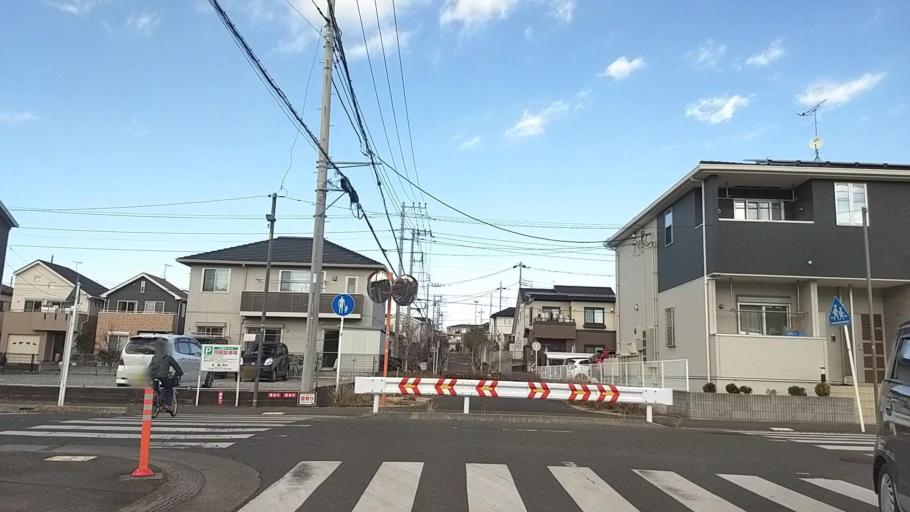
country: JP
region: Kanagawa
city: Isehara
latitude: 35.4098
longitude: 139.3210
